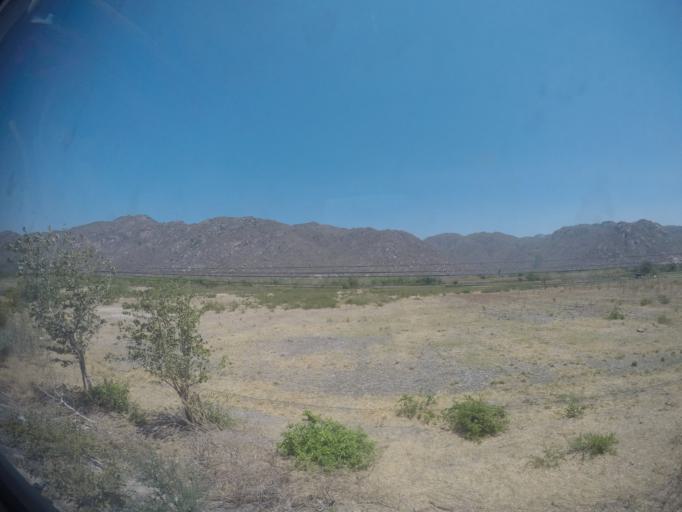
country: VN
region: Binh Thuan
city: Lien Huong
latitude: 11.3339
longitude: 108.7852
